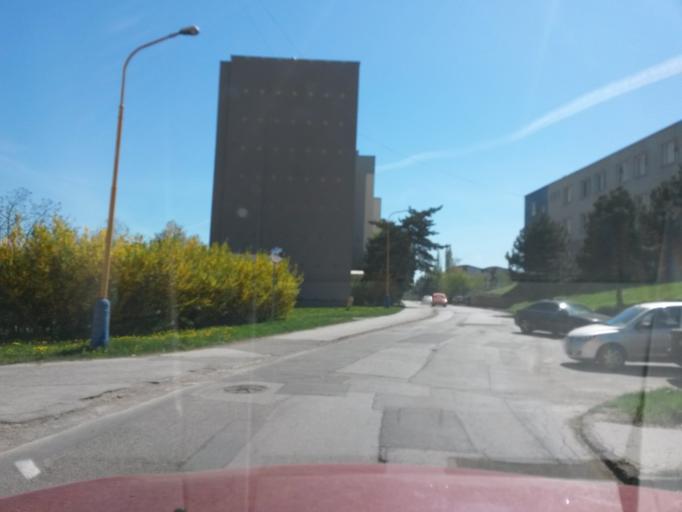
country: SK
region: Kosicky
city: Kosice
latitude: 48.7063
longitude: 21.2499
